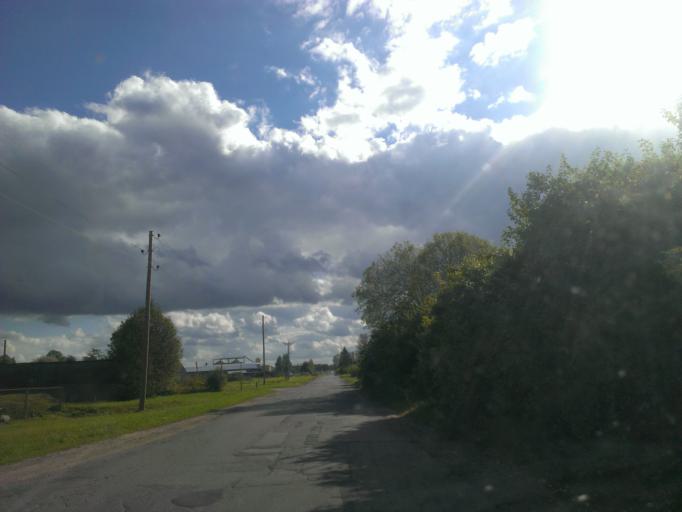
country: LV
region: Sigulda
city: Sigulda
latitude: 57.1465
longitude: 24.8923
